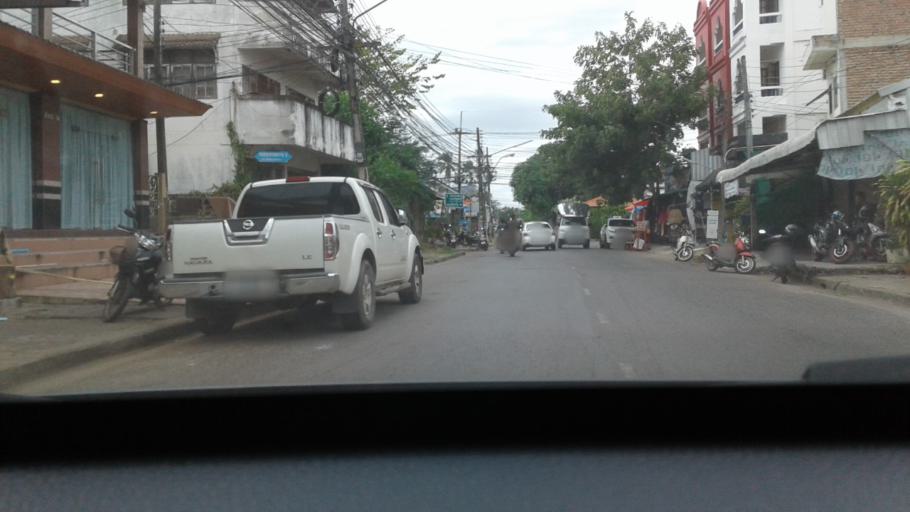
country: TH
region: Changwat Udon Thani
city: Udon Thani
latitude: 17.3991
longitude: 102.7819
